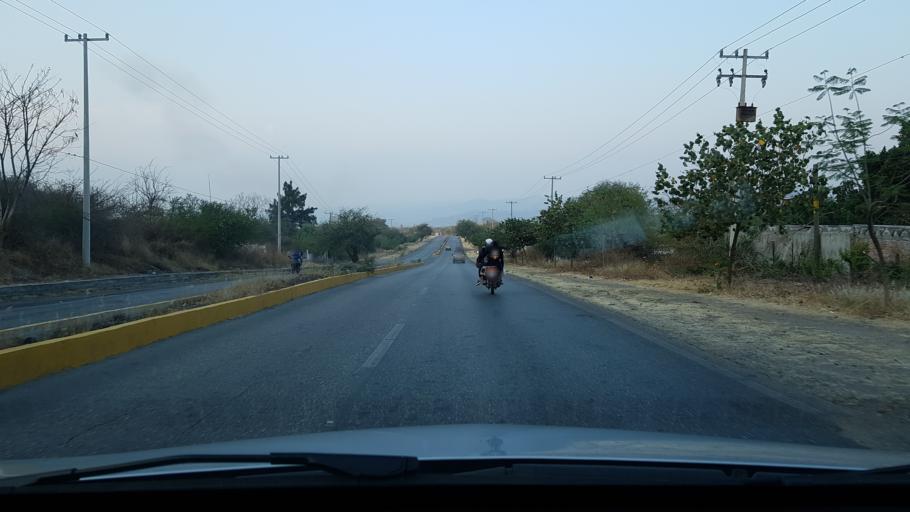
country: MX
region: Morelos
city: Jonacatepec de Leandro Valle
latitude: 18.6659
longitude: -98.8085
